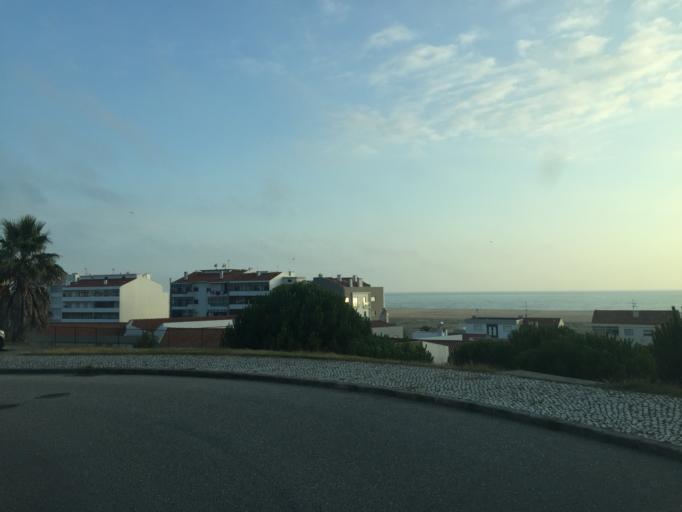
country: PT
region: Coimbra
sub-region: Figueira da Foz
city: Buarcos
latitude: 40.1601
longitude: -8.8683
